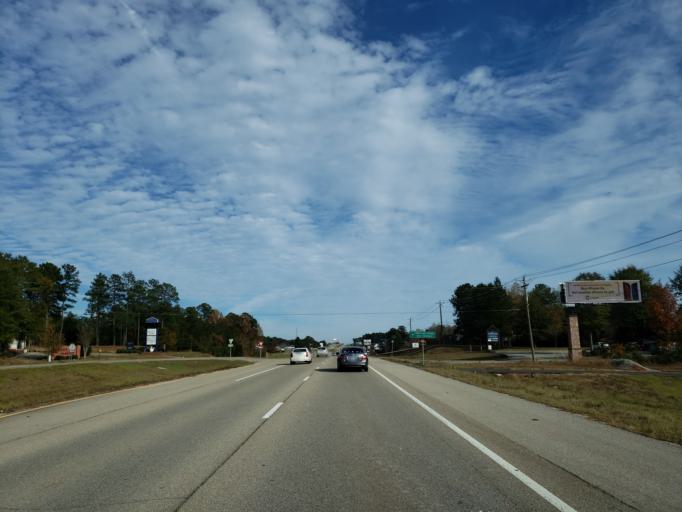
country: US
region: Mississippi
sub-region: Lamar County
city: West Hattiesburg
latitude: 31.3158
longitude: -89.4369
